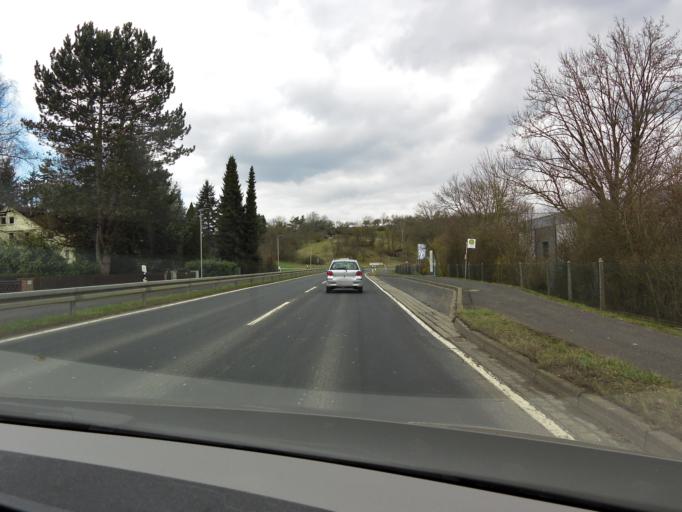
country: DE
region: Bavaria
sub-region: Regierungsbezirk Unterfranken
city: Rimpar
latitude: 49.8481
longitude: 9.9574
